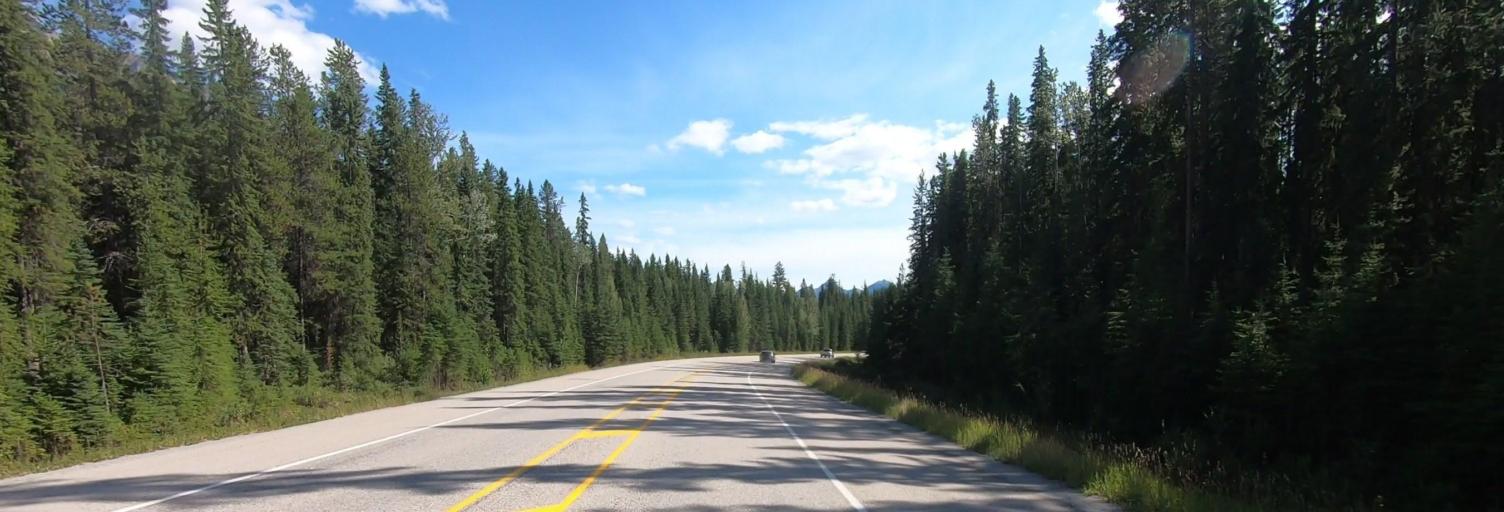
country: CA
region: Alberta
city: Lake Louise
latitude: 51.2242
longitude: -116.5736
